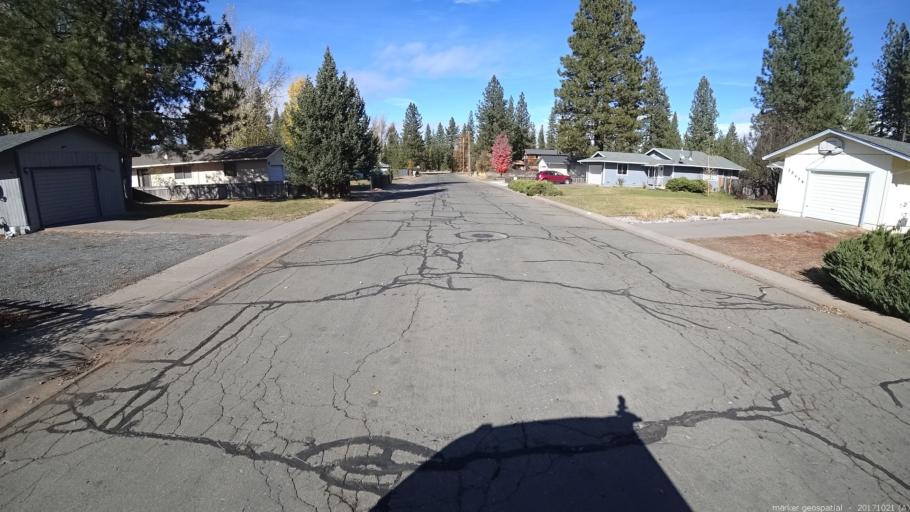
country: US
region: California
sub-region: Shasta County
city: Burney
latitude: 40.8836
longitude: -121.6478
